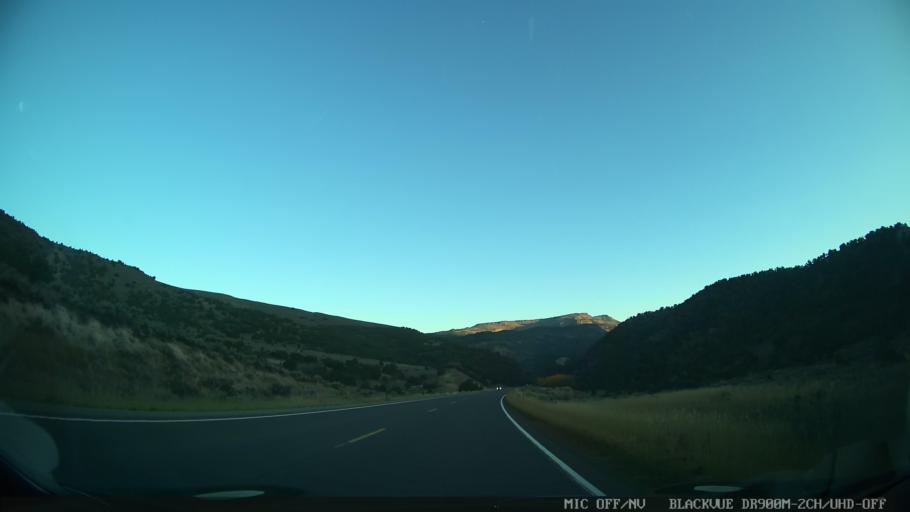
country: US
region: Colorado
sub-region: Eagle County
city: Edwards
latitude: 39.8422
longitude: -106.6421
